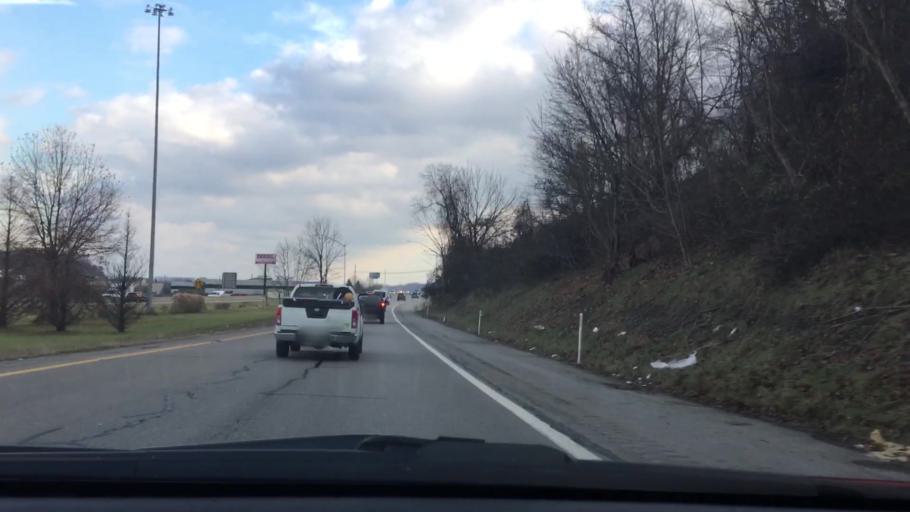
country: US
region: Pennsylvania
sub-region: Allegheny County
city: Oakdale
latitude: 40.4460
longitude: -80.1663
